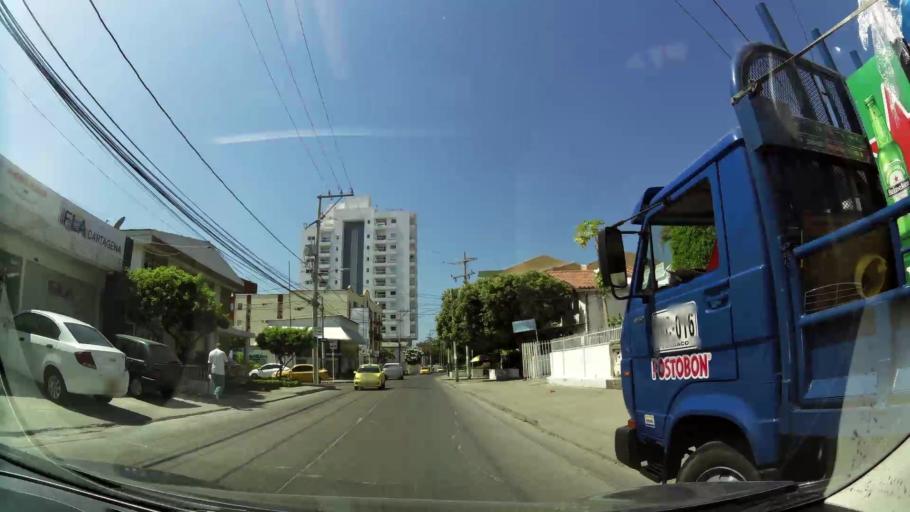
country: CO
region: Bolivar
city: Cartagena
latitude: 10.4166
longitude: -75.5302
